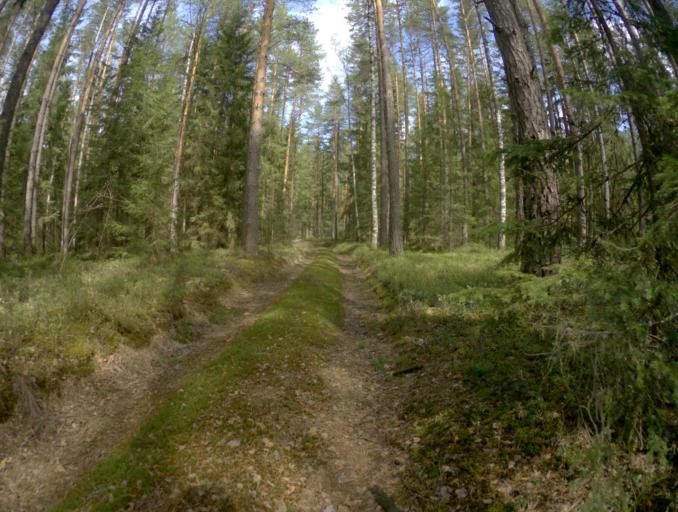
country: RU
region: Vladimir
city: Golovino
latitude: 55.9273
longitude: 40.3666
